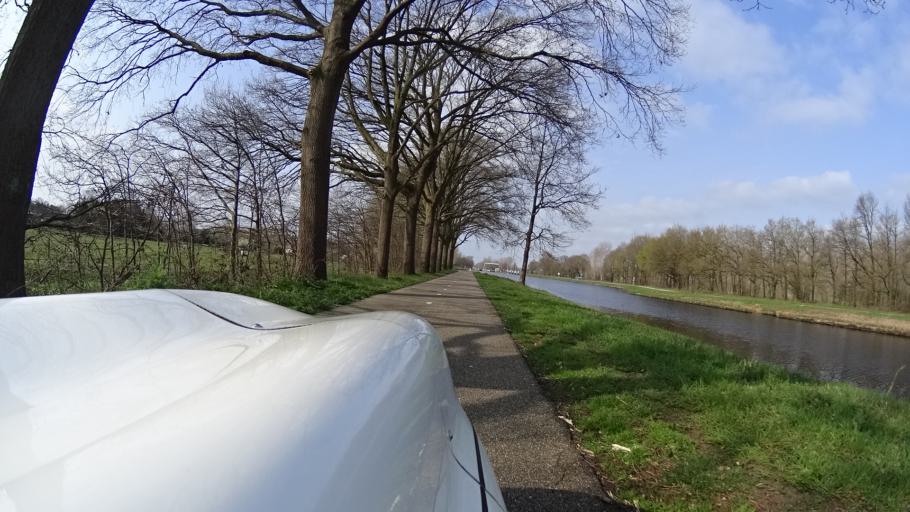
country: NL
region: North Brabant
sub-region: Gemeente Nuenen, Gerwen en Nederwetten
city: Nuenen
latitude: 51.5125
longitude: 5.5737
